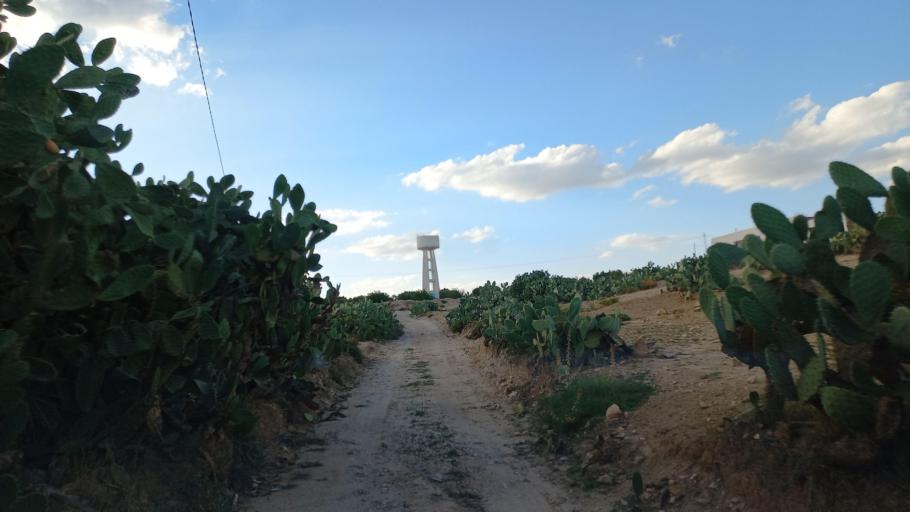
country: TN
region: Al Qasrayn
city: Sbiba
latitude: 35.3889
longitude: 9.0469
